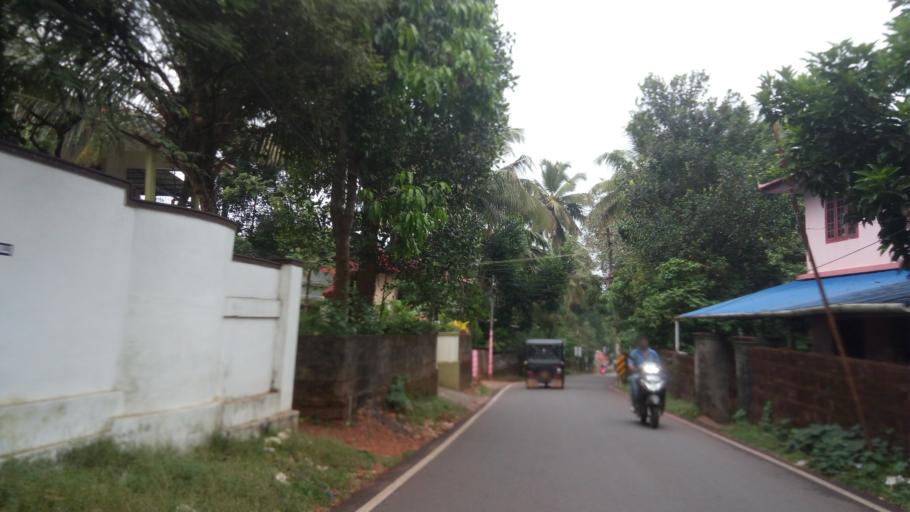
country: IN
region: Kerala
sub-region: Malappuram
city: Malappuram
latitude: 10.9885
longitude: 76.0074
